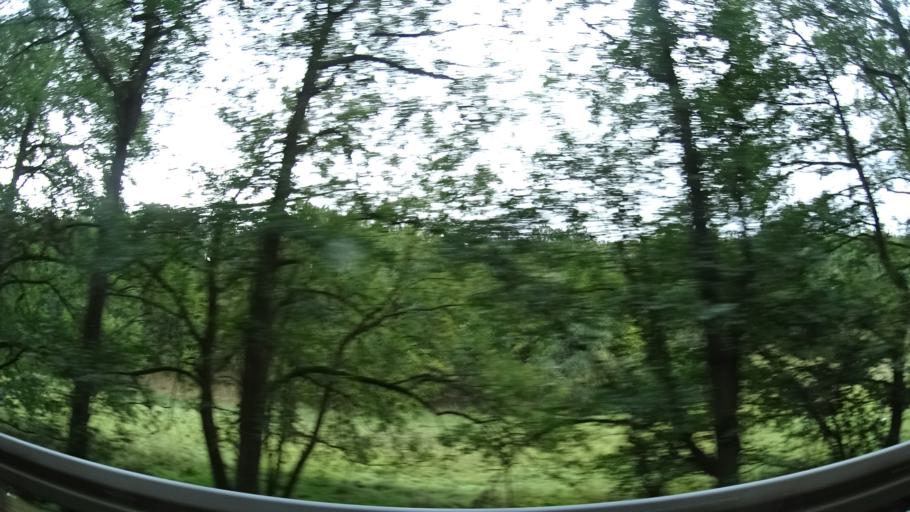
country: DE
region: Thuringia
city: Wahns
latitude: 50.6286
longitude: 10.3128
